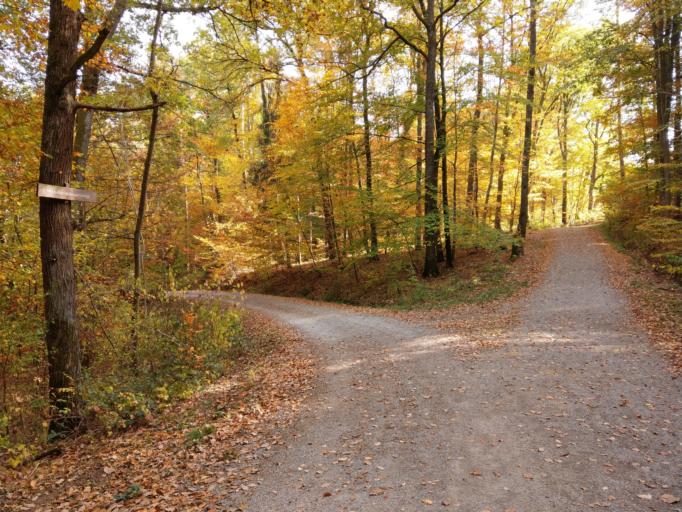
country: DE
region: Baden-Wuerttemberg
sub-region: Regierungsbezirk Stuttgart
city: Filderstadt
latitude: 48.6372
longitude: 9.2098
